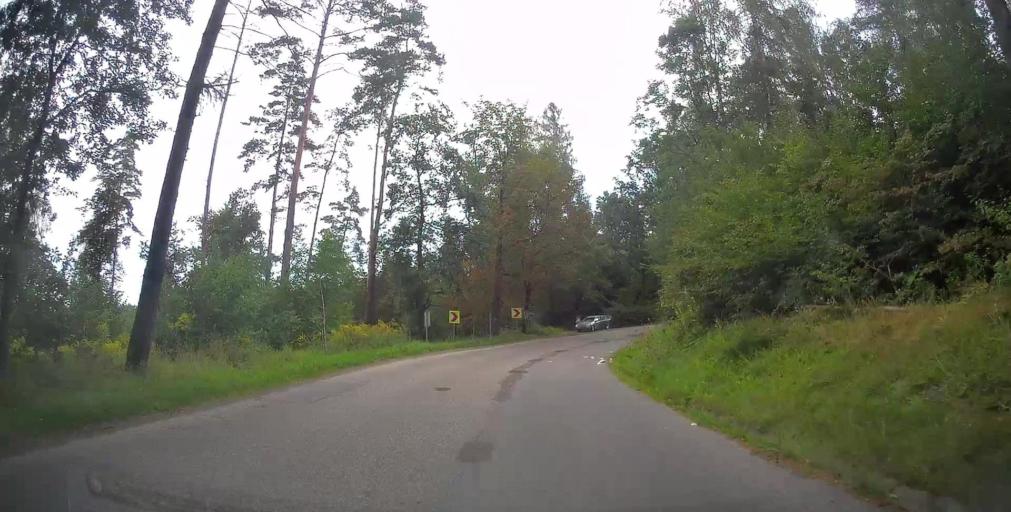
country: PL
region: Lesser Poland Voivodeship
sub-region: Powiat chrzanowski
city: Alwernia
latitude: 50.0726
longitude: 19.5488
